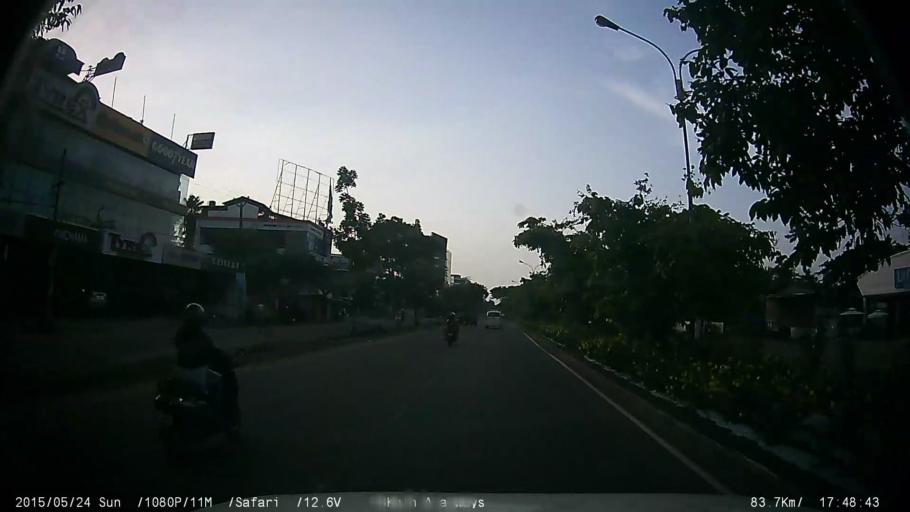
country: IN
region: Kerala
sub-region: Ernakulam
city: Cochin
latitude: 9.9845
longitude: 76.3164
